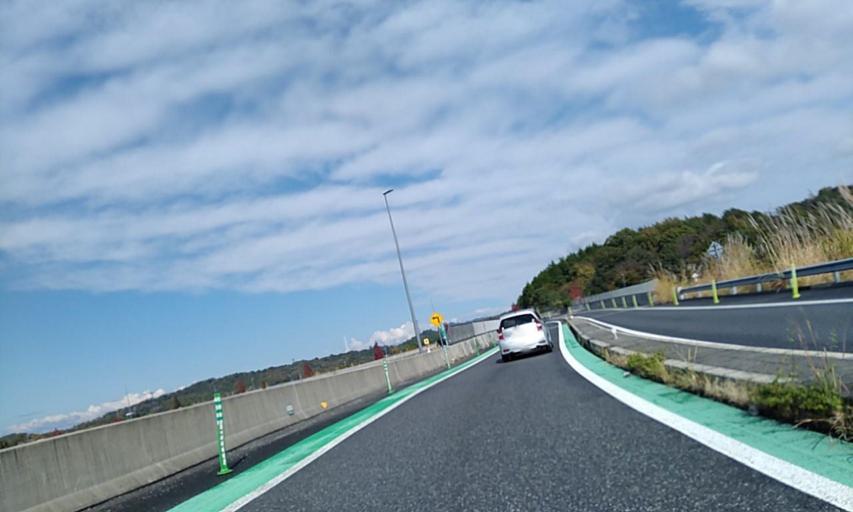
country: JP
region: Aichi
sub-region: Toyota-shi
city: Toyota
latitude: 35.0315
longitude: 137.2203
